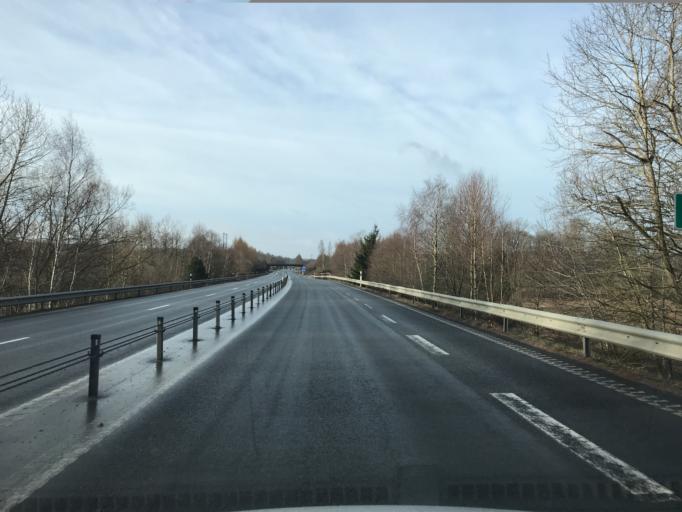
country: SE
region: Skane
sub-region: Hassleholms Kommun
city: Tormestorp
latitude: 56.1779
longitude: 13.6950
